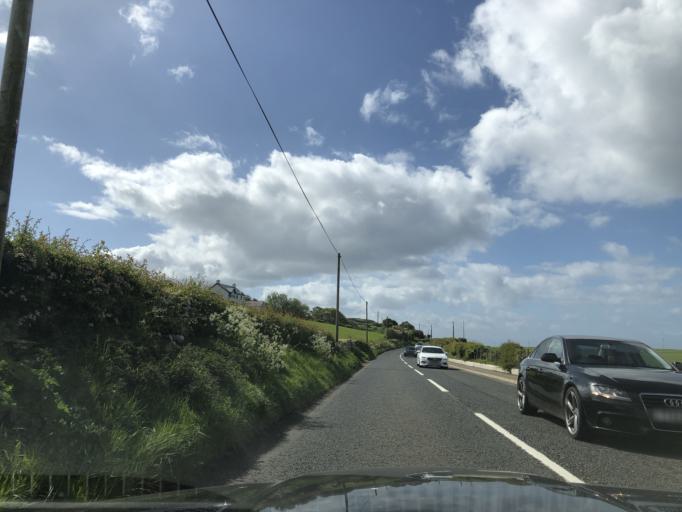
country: GB
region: Northern Ireland
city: Bushmills
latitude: 55.2101
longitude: -6.5506
